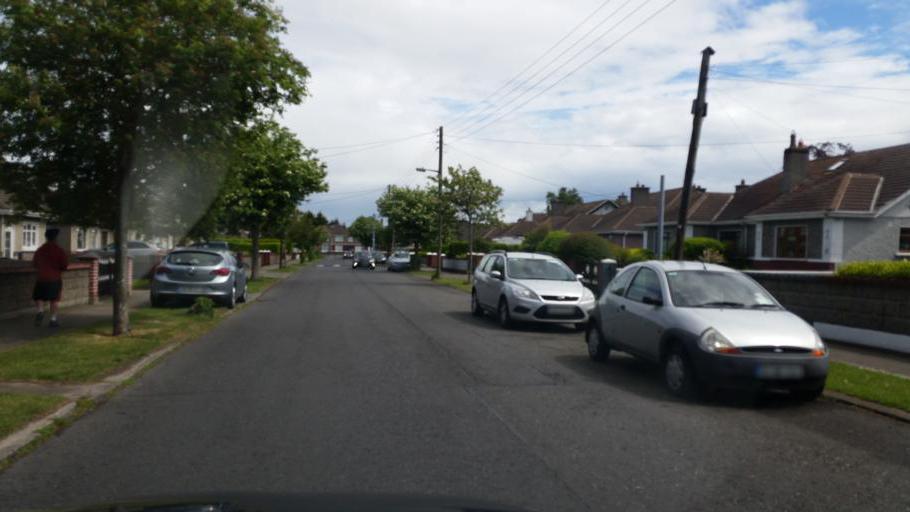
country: IE
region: Leinster
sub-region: Dublin City
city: Finglas
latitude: 53.3930
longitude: -6.2823
